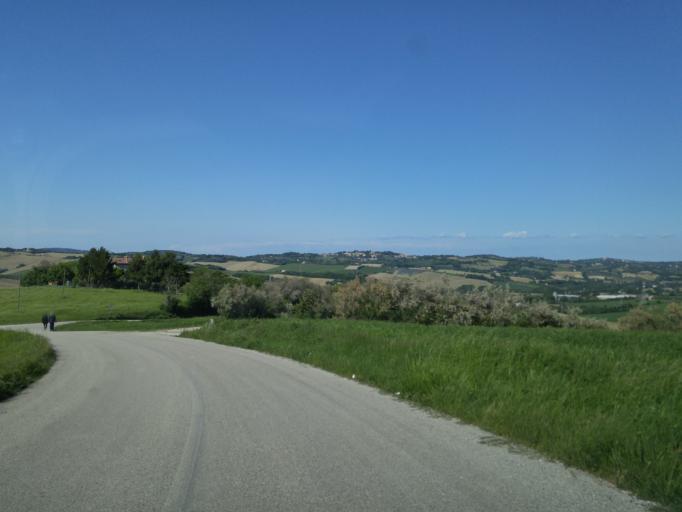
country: IT
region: The Marches
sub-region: Provincia di Pesaro e Urbino
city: Mombaroccio
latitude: 43.8218
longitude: 12.8504
